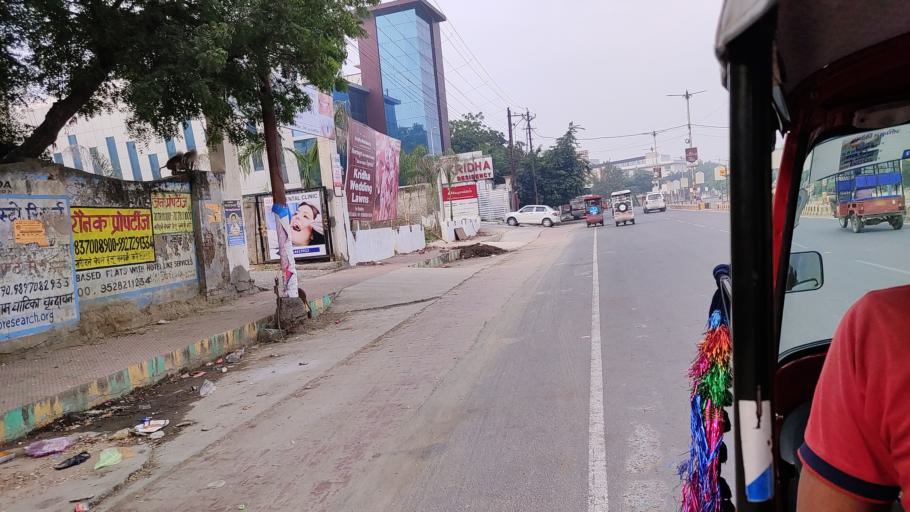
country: IN
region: Uttar Pradesh
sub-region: Mathura
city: Vrindavan
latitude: 27.5703
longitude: 77.6665
